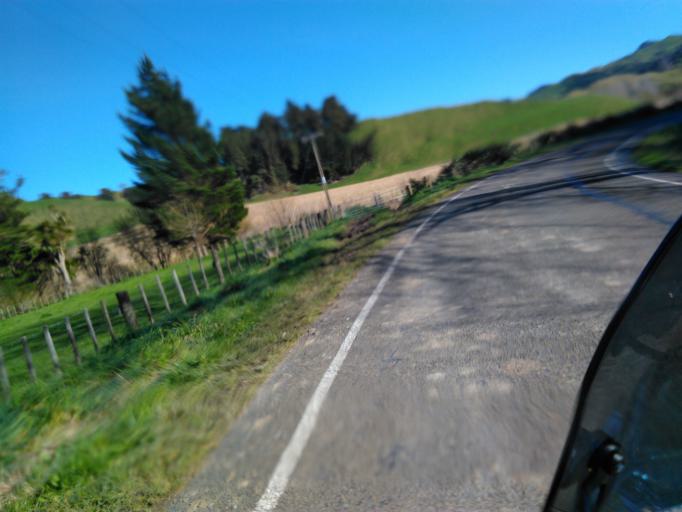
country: NZ
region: Gisborne
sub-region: Gisborne District
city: Gisborne
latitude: -38.4361
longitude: 177.7427
